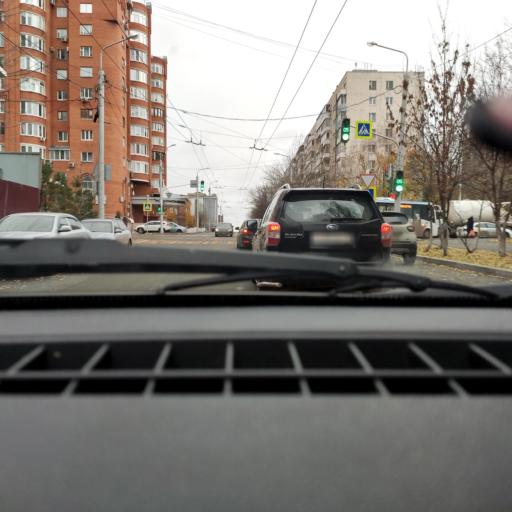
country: RU
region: Bashkortostan
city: Ufa
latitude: 54.7293
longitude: 55.9290
